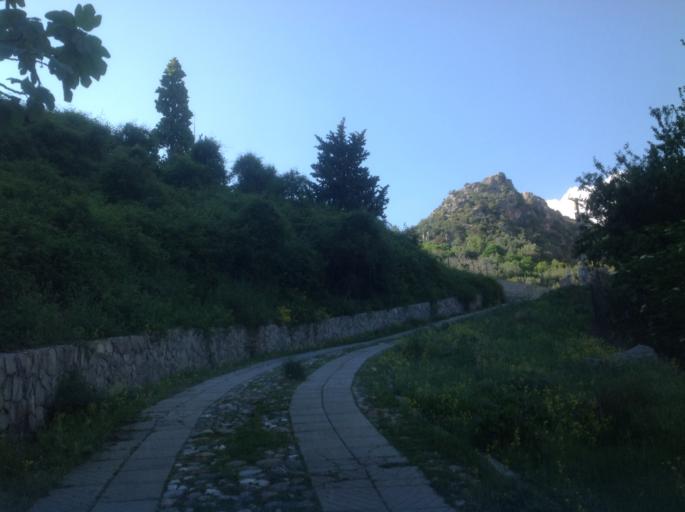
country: IT
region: Calabria
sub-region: Provincia di Cosenza
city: Civita
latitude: 39.8289
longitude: 16.3170
